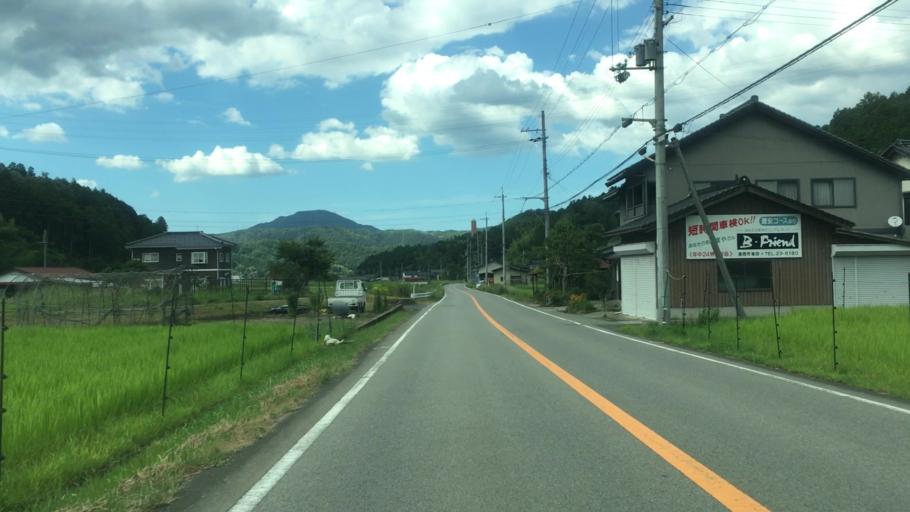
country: JP
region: Hyogo
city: Toyooka
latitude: 35.5368
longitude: 134.7898
